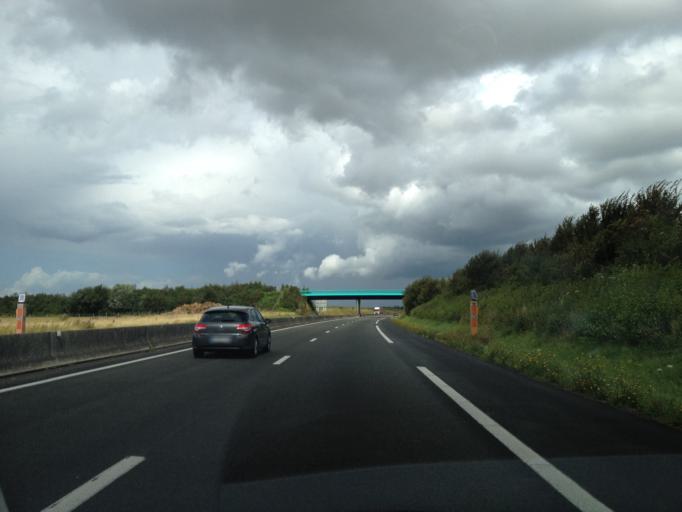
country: FR
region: Picardie
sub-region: Departement de la Somme
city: Sailly-Flibeaucourt
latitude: 50.1785
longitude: 1.7525
